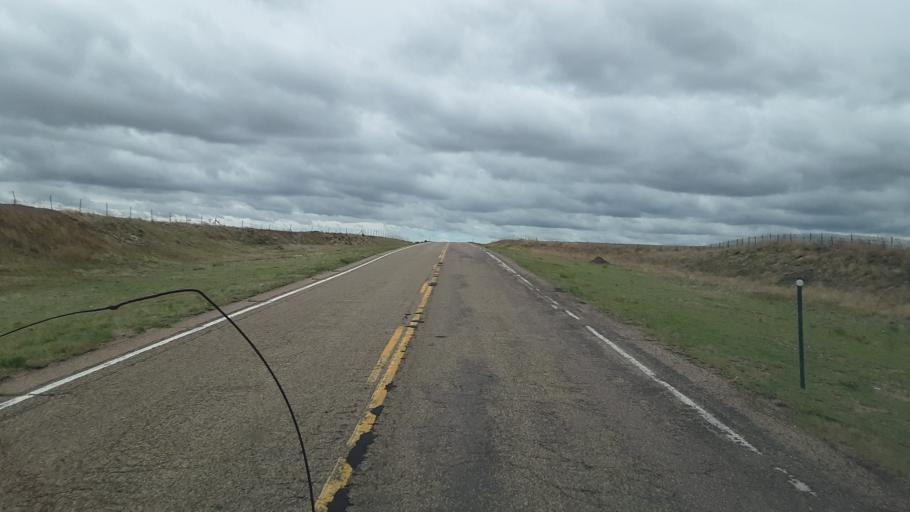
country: US
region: Colorado
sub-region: Lincoln County
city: Limon
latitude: 38.8393
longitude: -103.9089
